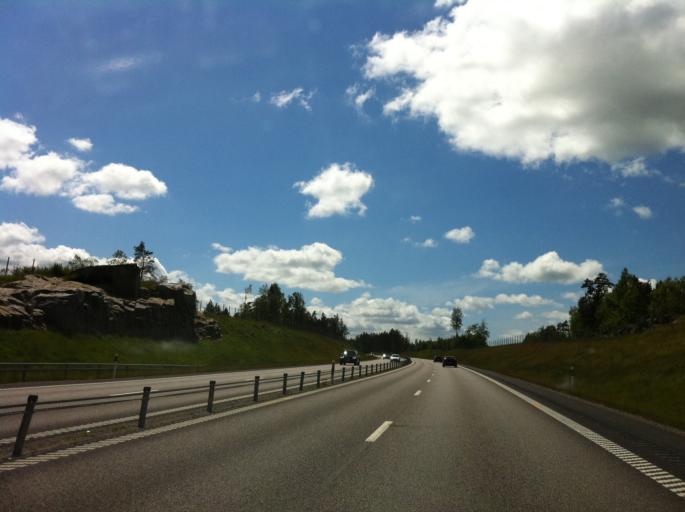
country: SE
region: Vaestra Goetaland
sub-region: Trollhattan
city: Sjuntorp
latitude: 58.2370
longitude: 12.2321
